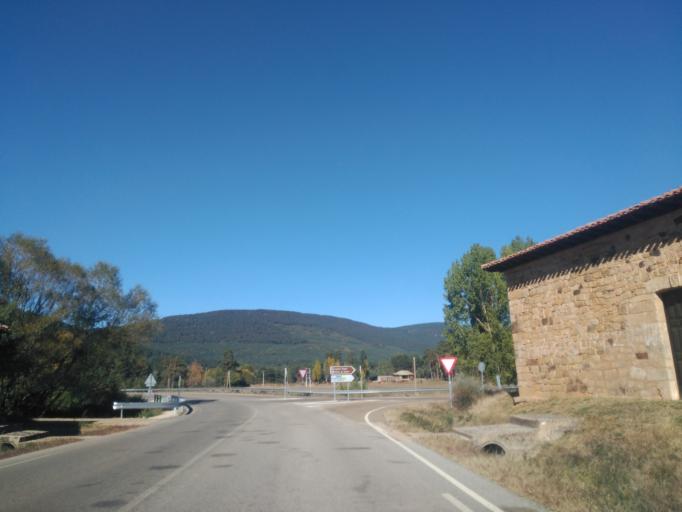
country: ES
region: Castille and Leon
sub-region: Provincia de Soria
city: Vinuesa
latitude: 41.9117
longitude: -2.7548
